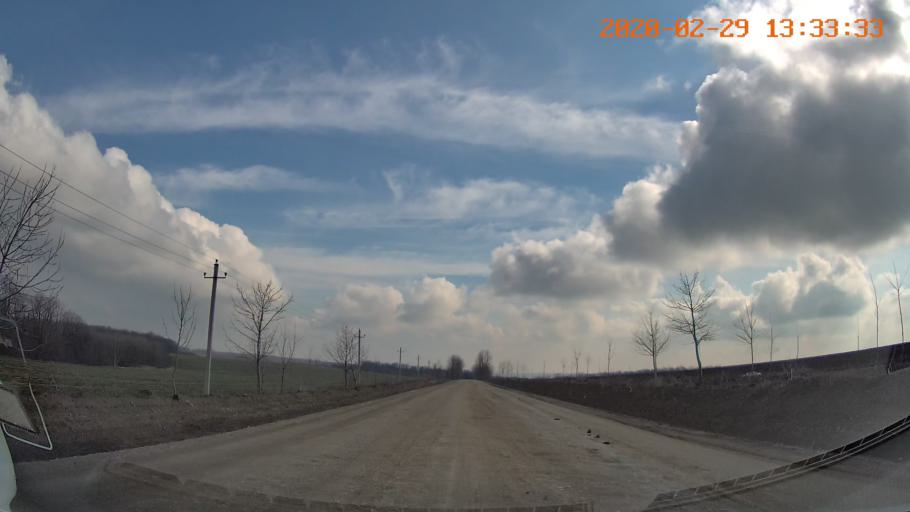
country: MD
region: Telenesti
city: Camenca
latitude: 47.8730
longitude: 28.6172
